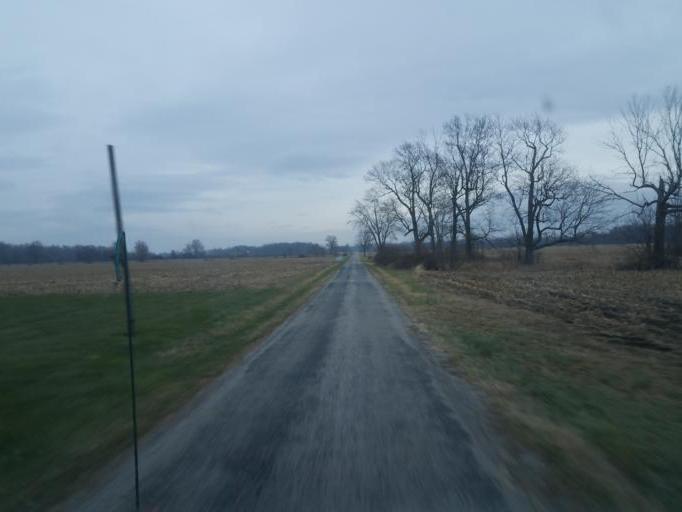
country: US
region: Ohio
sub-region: Marion County
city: Marion
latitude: 40.5532
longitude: -83.0324
